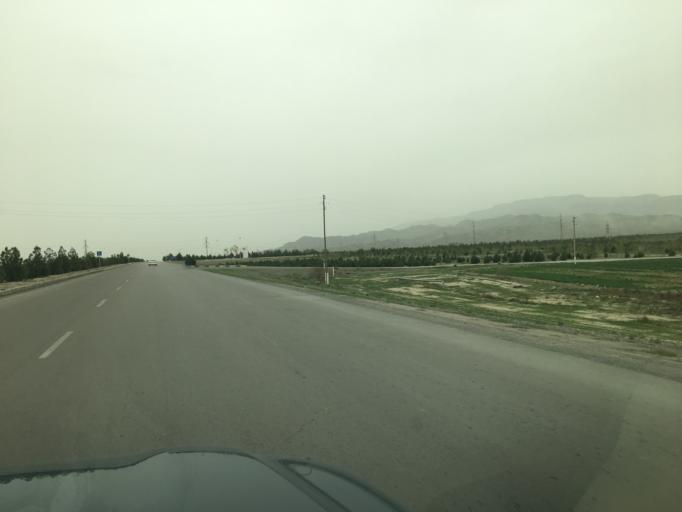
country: TM
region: Ahal
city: Baharly
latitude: 38.2854
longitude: 57.6596
